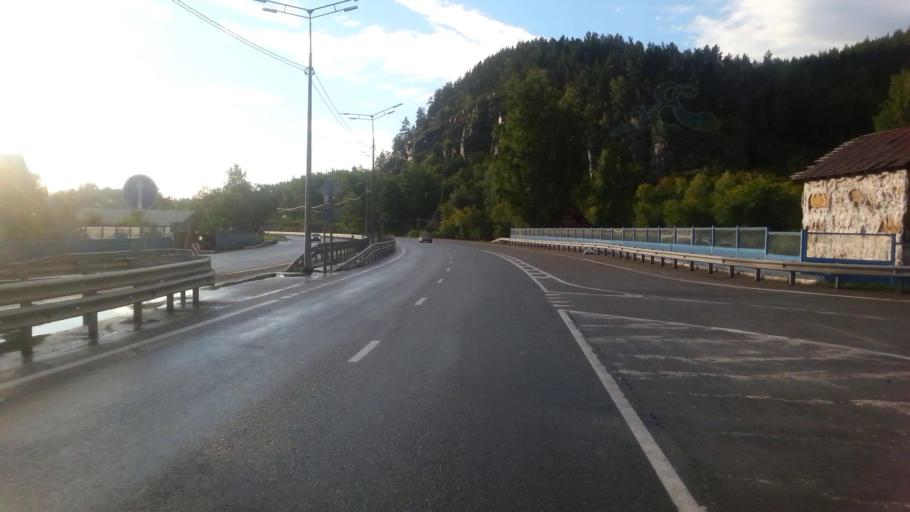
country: RU
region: Altay
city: Souzga
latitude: 51.9181
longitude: 85.8592
